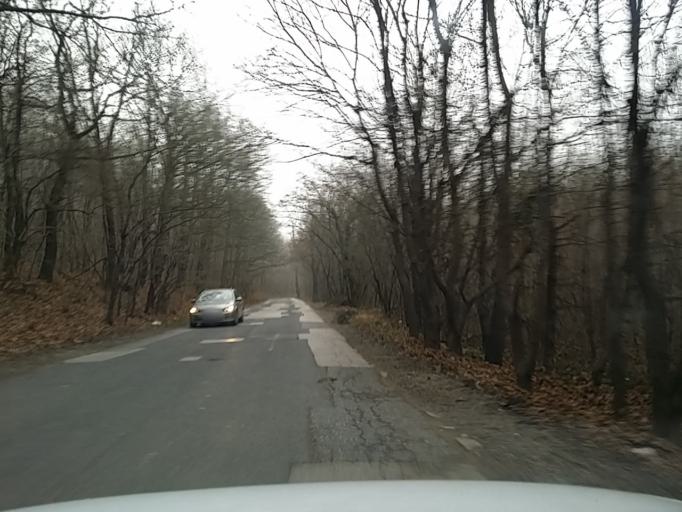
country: HU
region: Pest
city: Budakeszi
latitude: 47.5357
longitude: 18.9478
